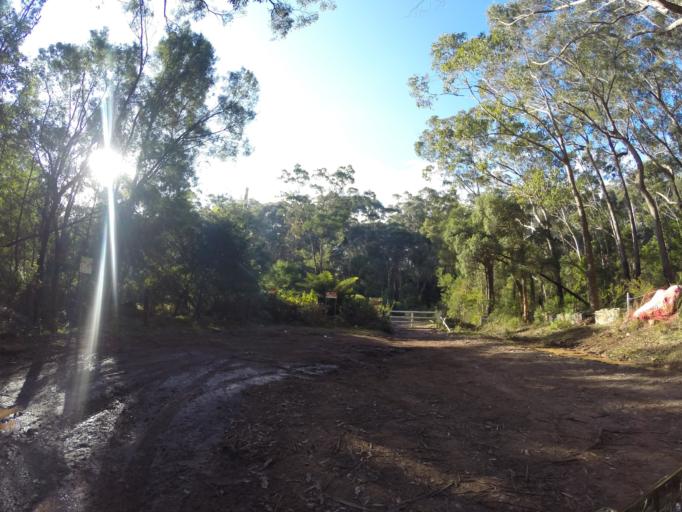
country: AU
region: New South Wales
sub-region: Wollongong
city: Cordeaux Heights
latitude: -34.4066
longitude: 150.7859
